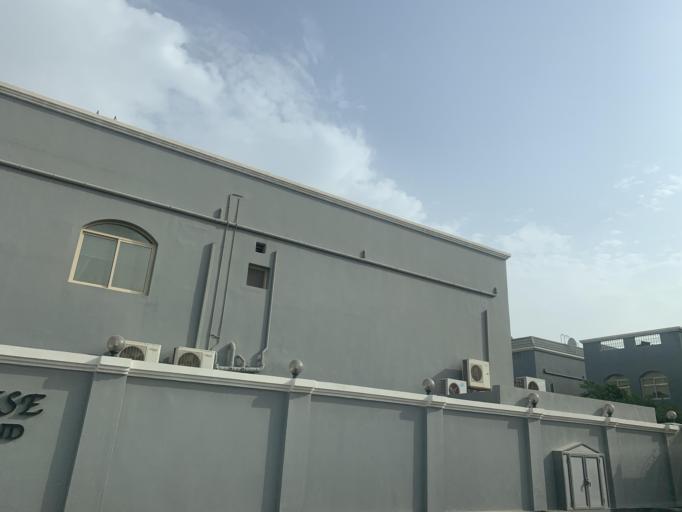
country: BH
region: Northern
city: Madinat `Isa
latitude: 26.1768
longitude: 50.4863
